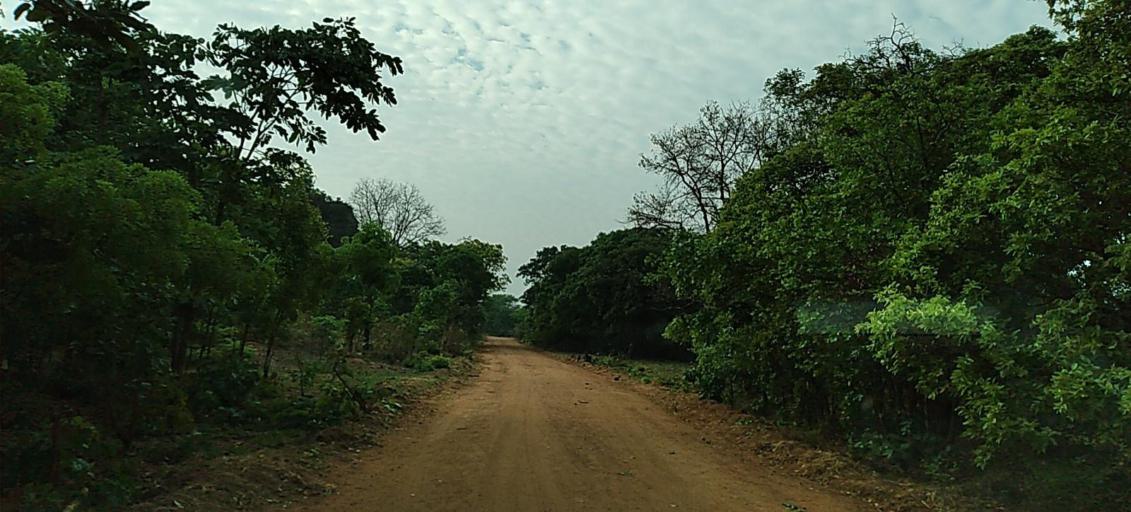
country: ZM
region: Copperbelt
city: Kalulushi
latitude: -12.9067
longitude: 27.6883
